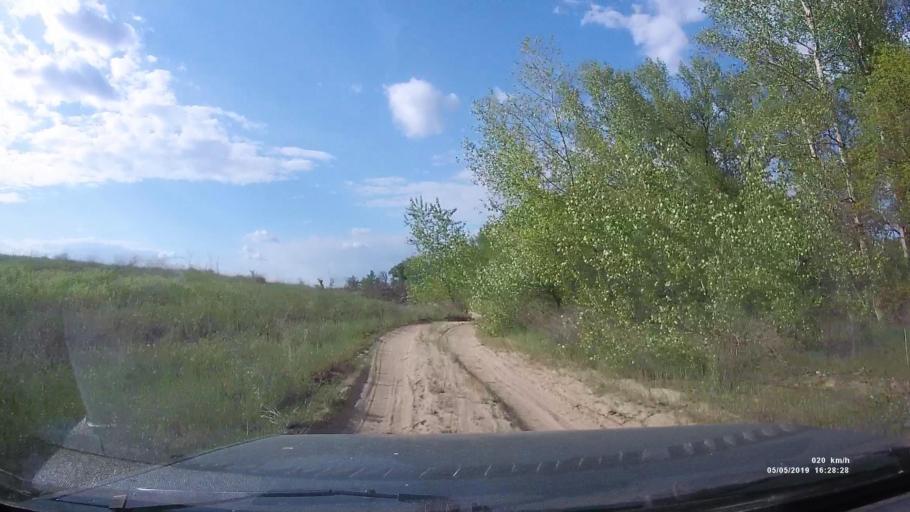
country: RU
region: Rostov
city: Ust'-Donetskiy
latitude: 47.7676
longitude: 41.0158
